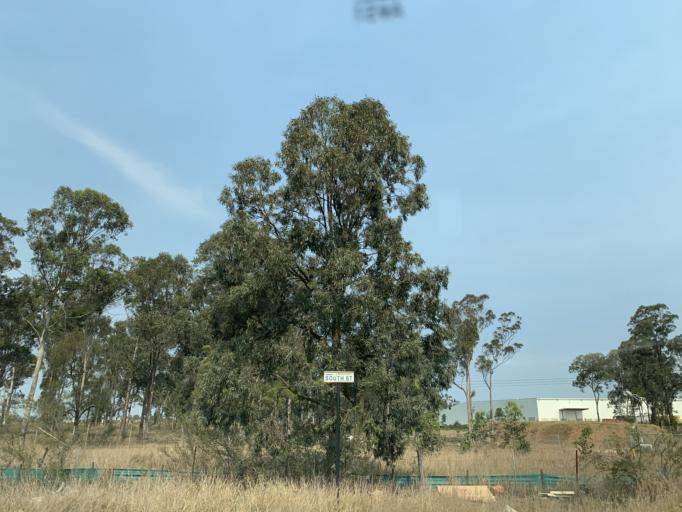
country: AU
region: New South Wales
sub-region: Blacktown
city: Hassall Grove
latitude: -33.7122
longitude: 150.8210
